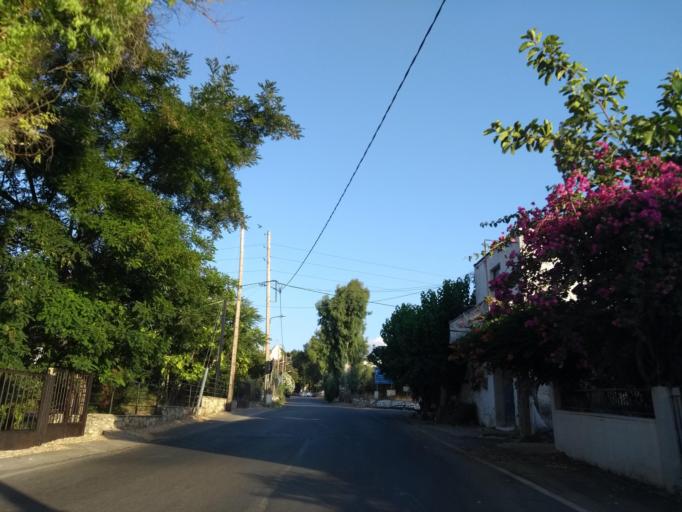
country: GR
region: Crete
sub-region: Nomos Chanias
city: Kalivai
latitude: 35.4110
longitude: 24.1962
